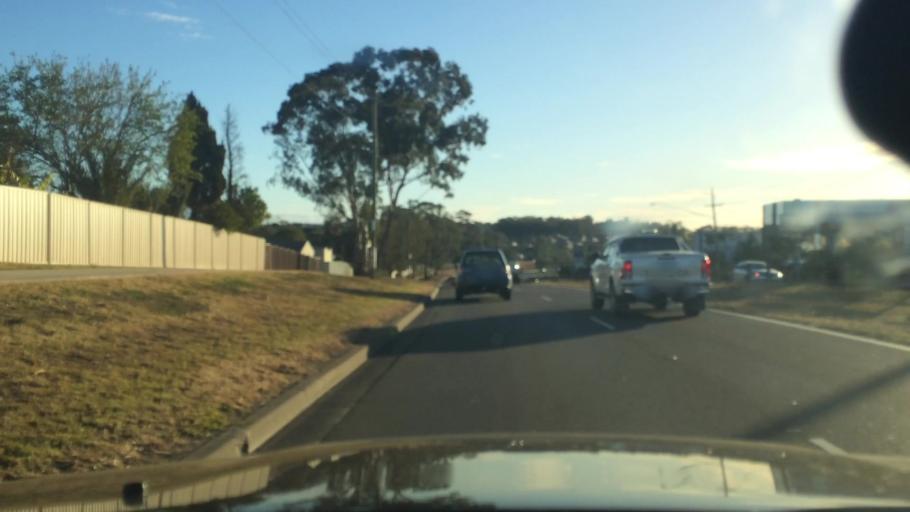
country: AU
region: New South Wales
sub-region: Fairfield
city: Horsley Park
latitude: -33.8526
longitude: 150.8912
